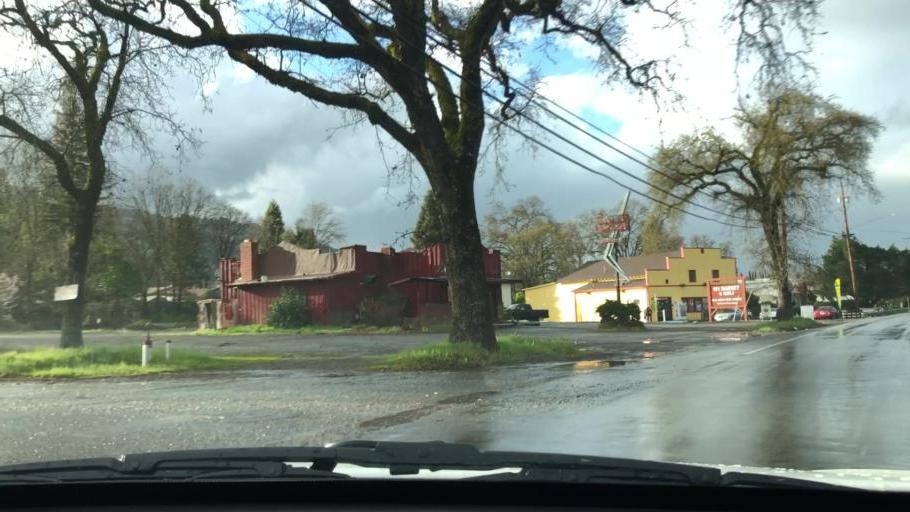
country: US
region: California
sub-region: Mendocino County
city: Ukiah
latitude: 39.1241
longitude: -123.2045
